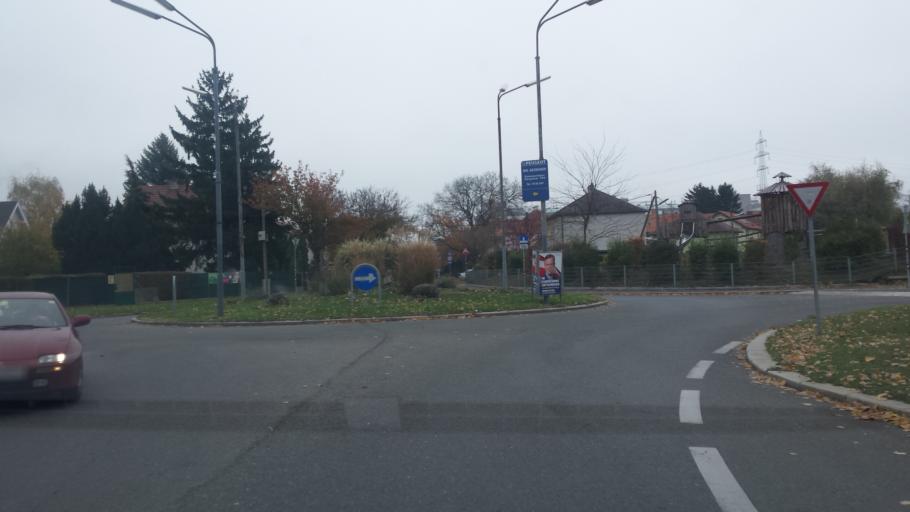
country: AT
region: Lower Austria
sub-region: Politischer Bezirk Wien-Umgebung
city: Schwechat
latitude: 48.1581
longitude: 16.4243
